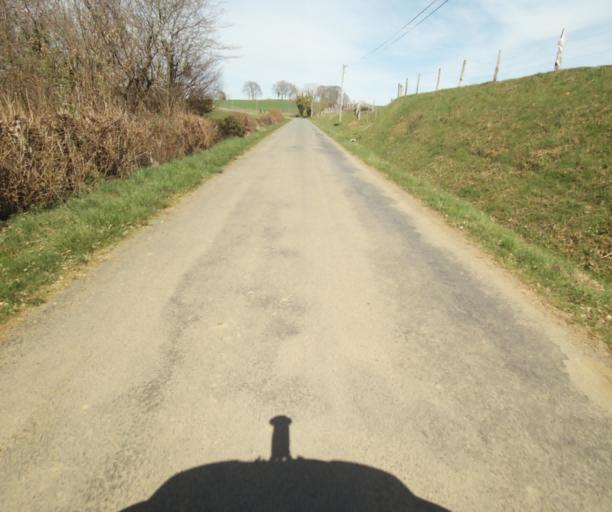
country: FR
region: Limousin
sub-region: Departement de la Correze
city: Seilhac
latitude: 45.3932
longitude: 1.7832
